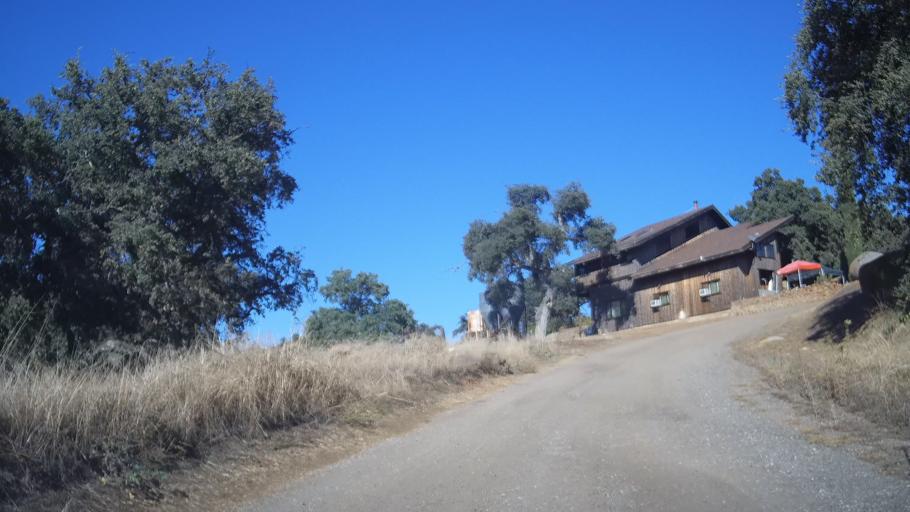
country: US
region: California
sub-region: San Diego County
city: San Diego Country Estates
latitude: 33.0697
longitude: -116.7579
